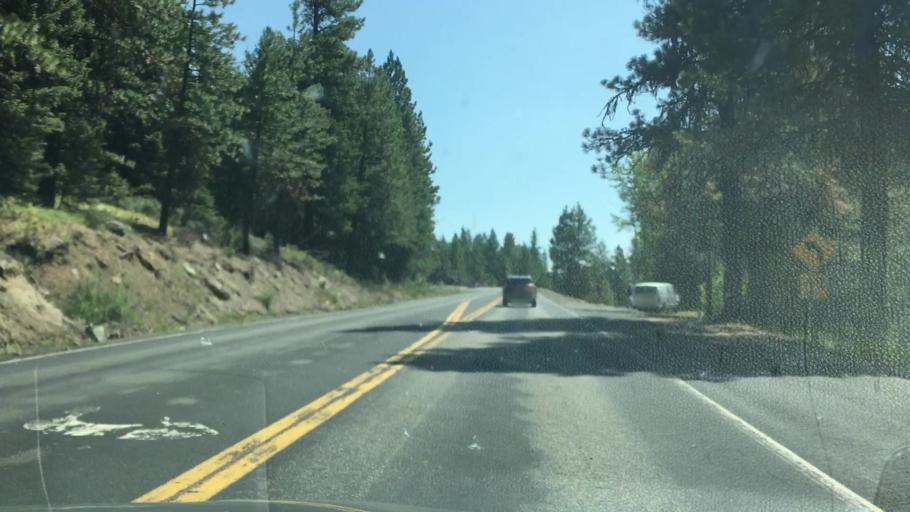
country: US
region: Idaho
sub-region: Valley County
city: McCall
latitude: 44.9335
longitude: -116.1652
